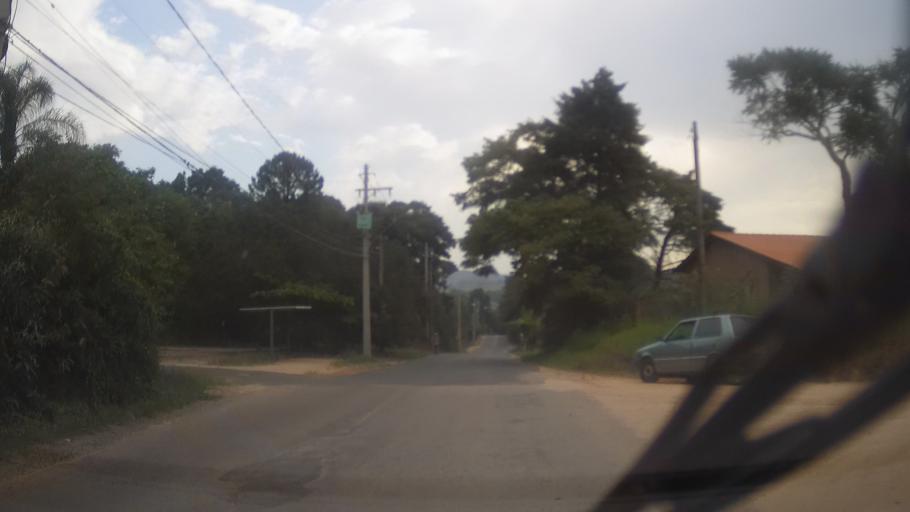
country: BR
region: Sao Paulo
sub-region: Itupeva
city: Itupeva
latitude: -23.1741
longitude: -47.1103
